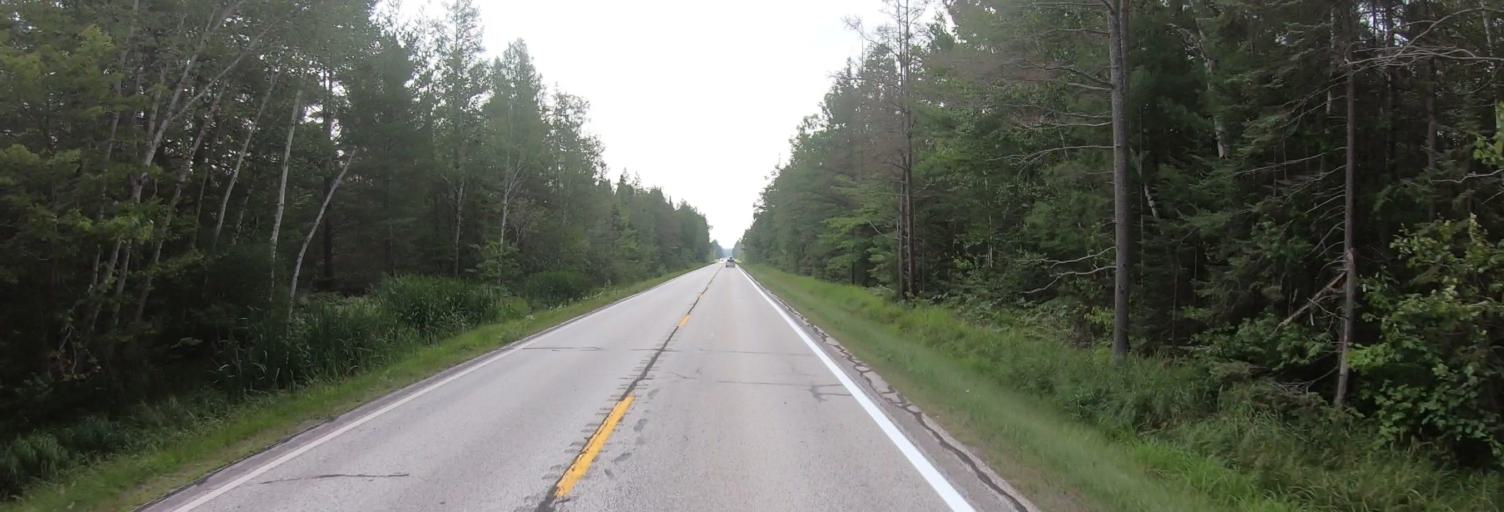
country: US
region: Michigan
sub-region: Luce County
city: Newberry
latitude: 46.4918
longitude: -85.4268
